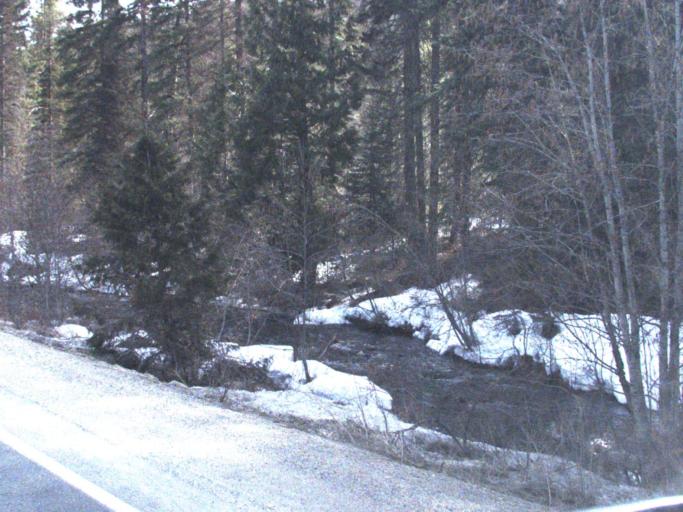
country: US
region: Washington
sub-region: Stevens County
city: Chewelah
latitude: 48.5338
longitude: -117.6128
